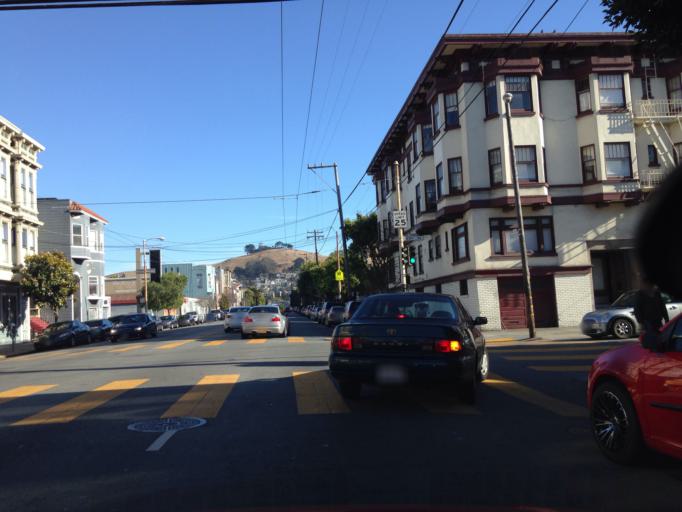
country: US
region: California
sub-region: San Francisco County
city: San Francisco
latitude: 37.7541
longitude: -122.4165
